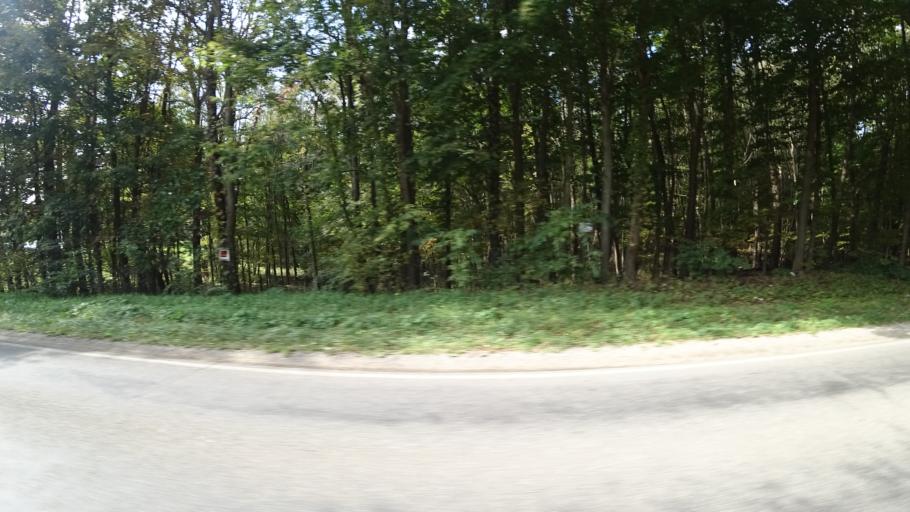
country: US
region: Michigan
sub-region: Saint Joseph County
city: Three Rivers
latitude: 41.9194
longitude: -85.6246
